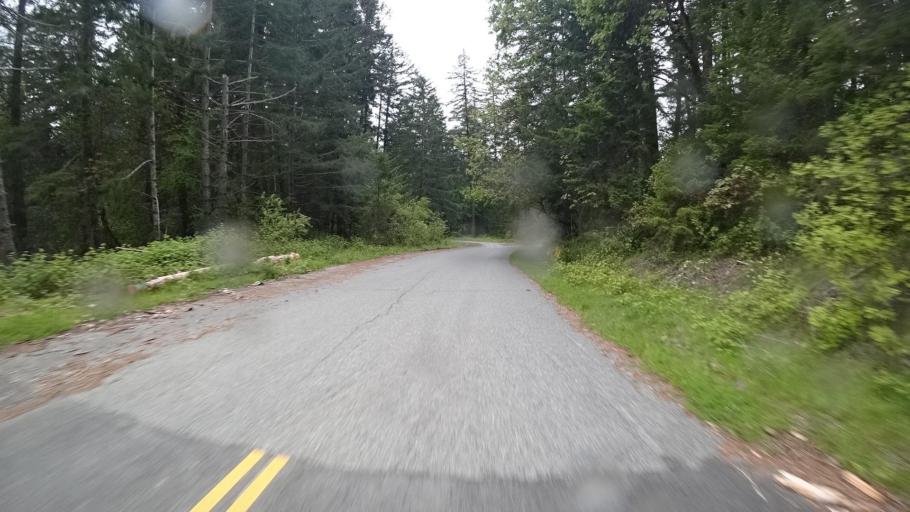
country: US
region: California
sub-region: Humboldt County
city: Willow Creek
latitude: 41.1235
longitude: -123.7468
